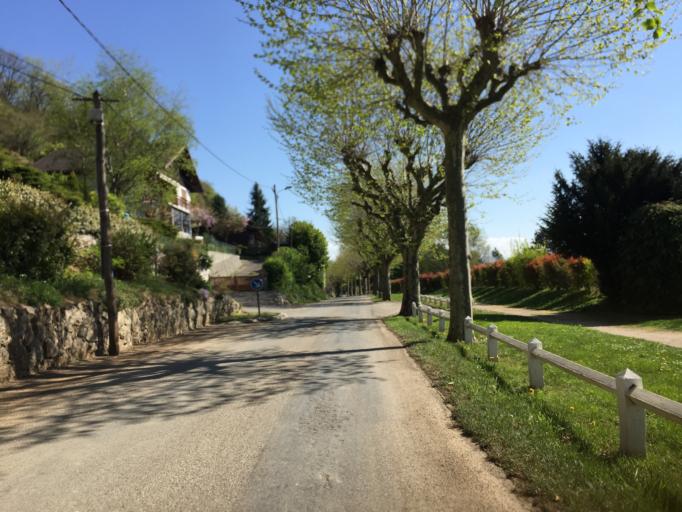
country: FR
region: Rhone-Alpes
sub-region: Departement de la Savoie
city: Barby
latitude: 45.5624
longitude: 5.9819
